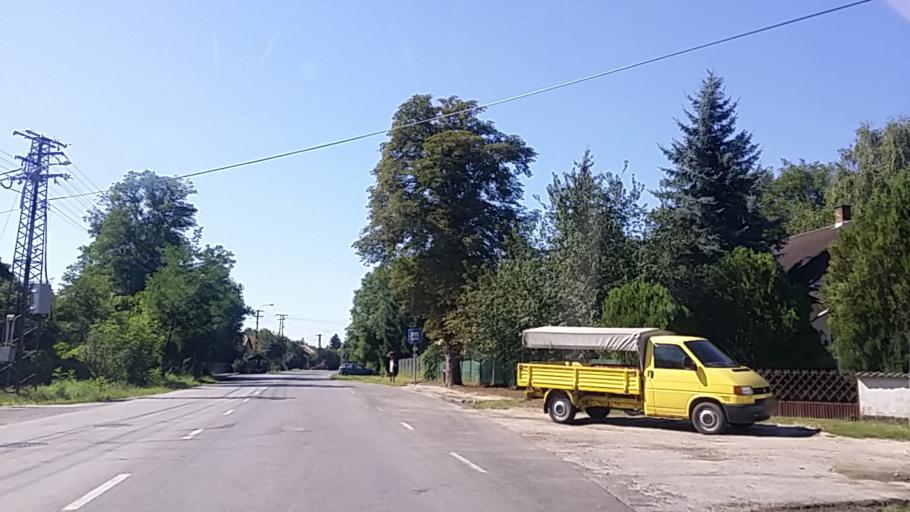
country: HU
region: Fejer
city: Cece
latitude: 46.7803
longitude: 18.6338
